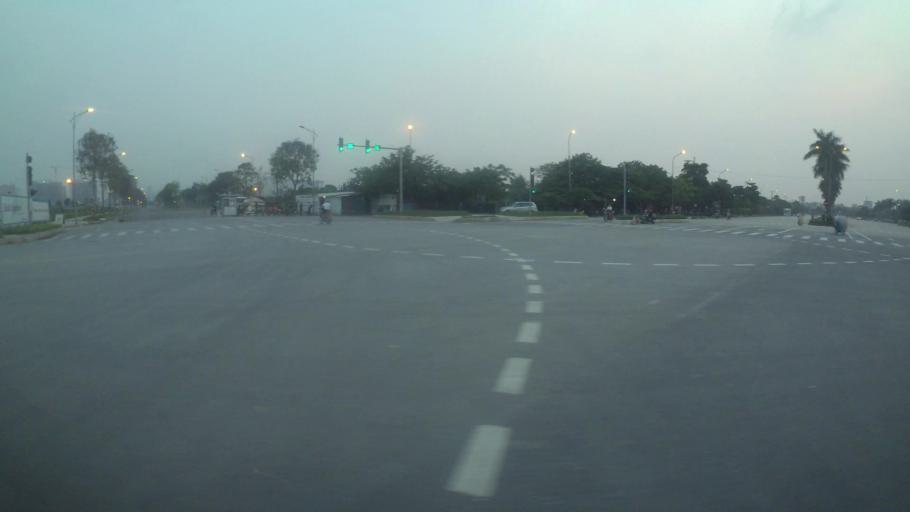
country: VN
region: Ha Noi
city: Tay Ho
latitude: 21.0626
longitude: 105.7901
